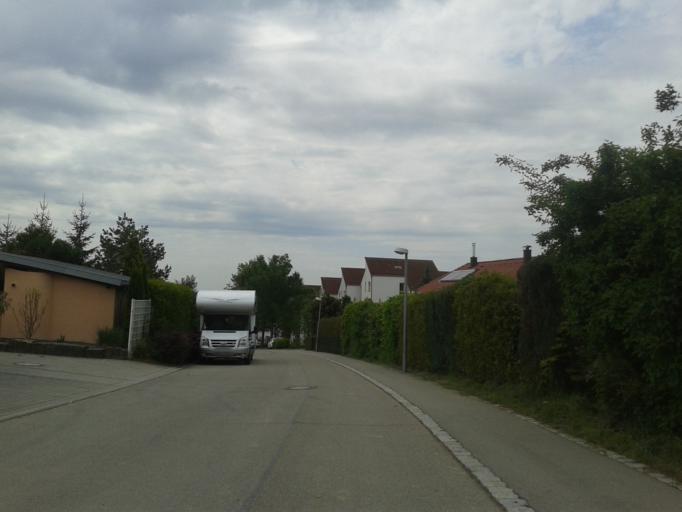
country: DE
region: Baden-Wuerttemberg
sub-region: Tuebingen Region
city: Erbach
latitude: 48.3353
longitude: 9.8981
